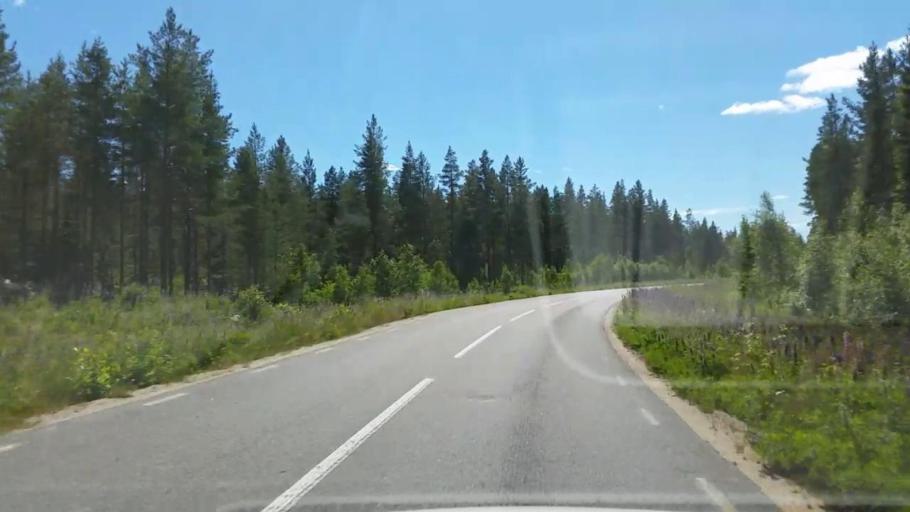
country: SE
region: Gaevleborg
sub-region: Ljusdals Kommun
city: Farila
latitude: 61.7249
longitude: 15.7261
